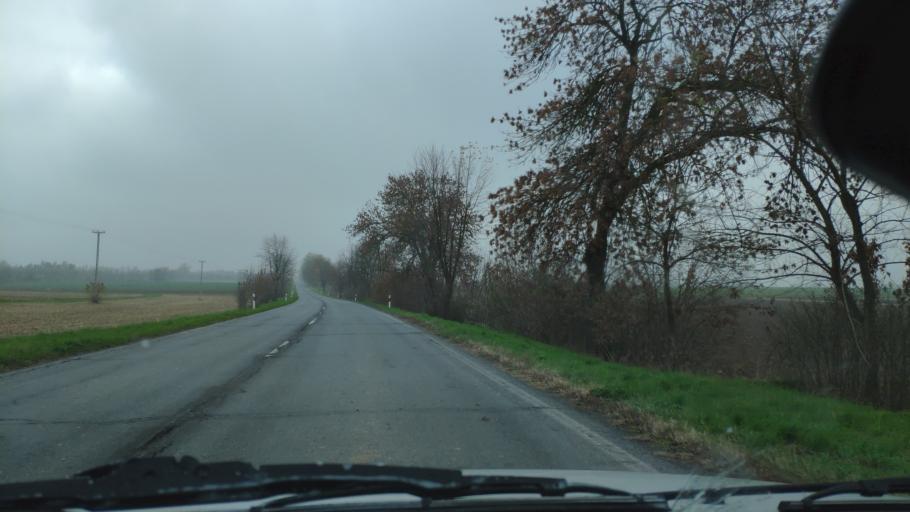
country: HU
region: Zala
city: Zalakomar
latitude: 46.5976
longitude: 17.2634
